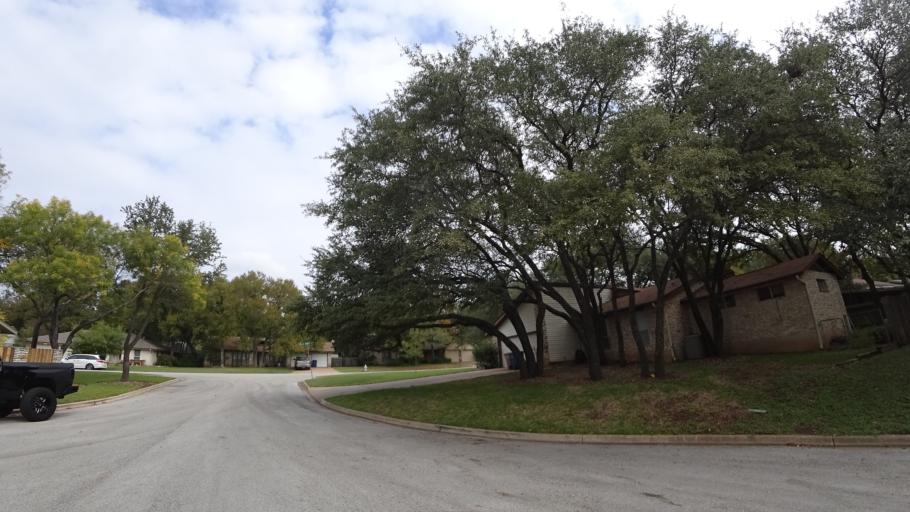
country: US
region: Texas
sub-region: Travis County
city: Wells Branch
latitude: 30.4286
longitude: -97.7107
